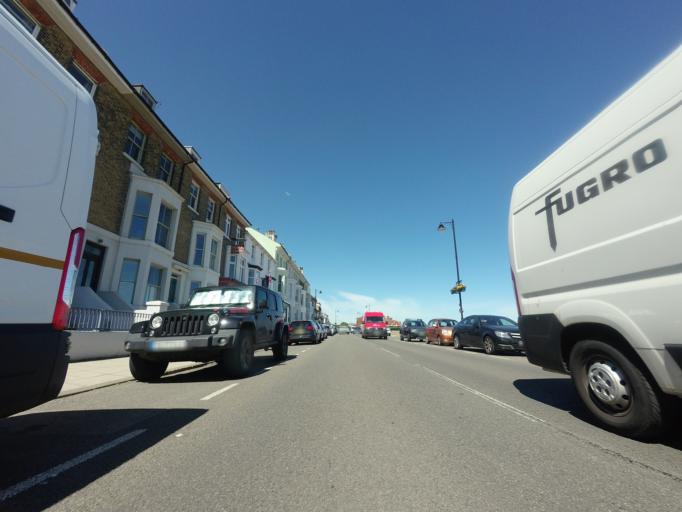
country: GB
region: England
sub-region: Kent
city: Deal
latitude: 51.2144
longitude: 1.4027
